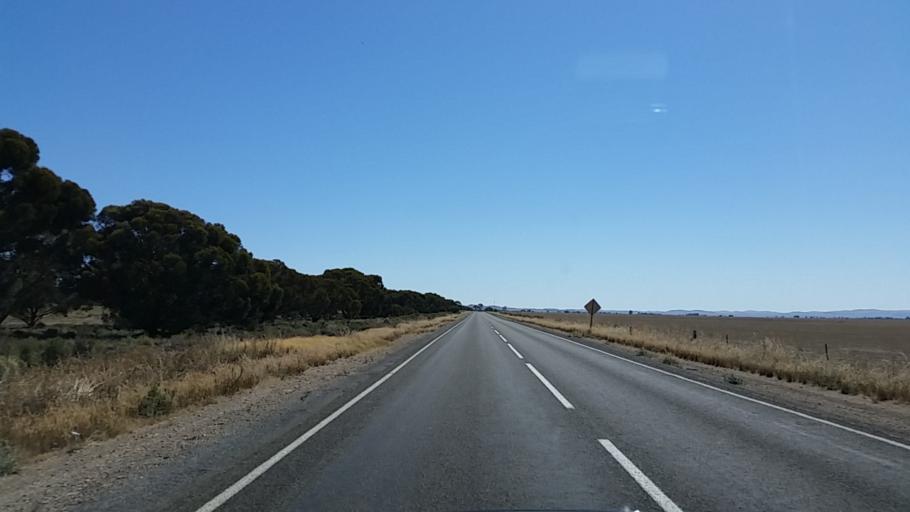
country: AU
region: South Australia
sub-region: Peterborough
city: Peterborough
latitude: -32.7573
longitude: 138.6478
